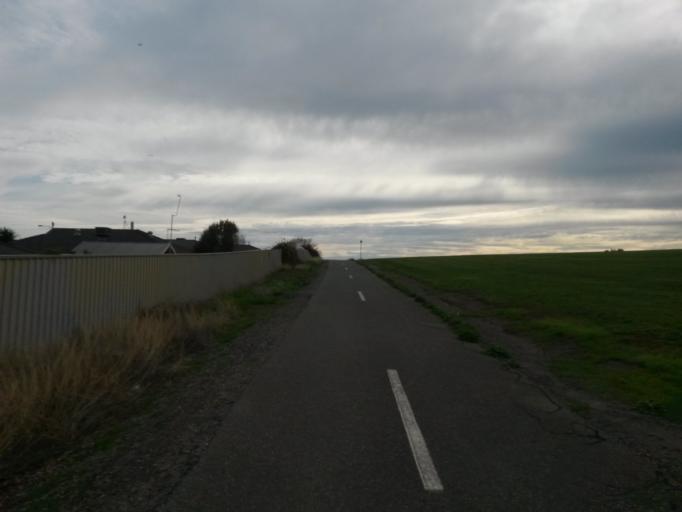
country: AU
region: South Australia
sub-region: Onkaparinga
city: Moana
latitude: -35.2062
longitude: 138.4903
